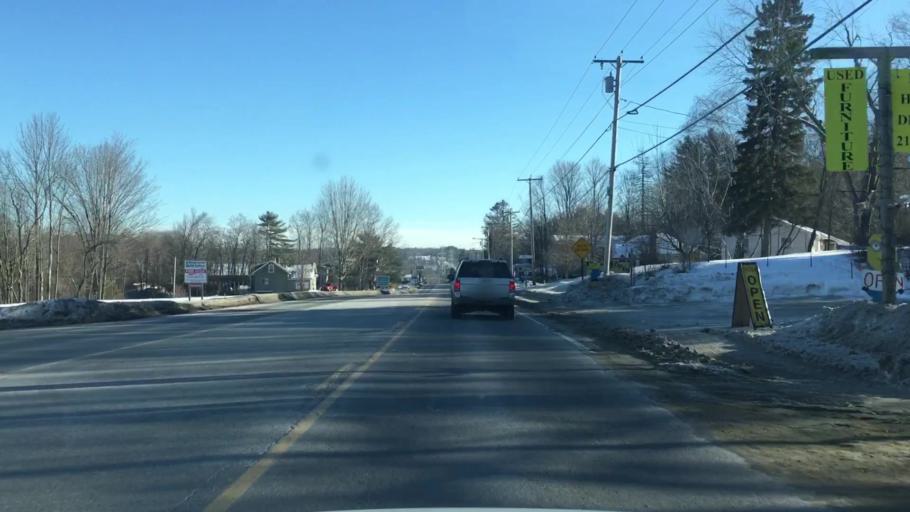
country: US
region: Maine
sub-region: Kennebec County
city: Farmingdale
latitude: 44.2625
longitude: -69.7814
